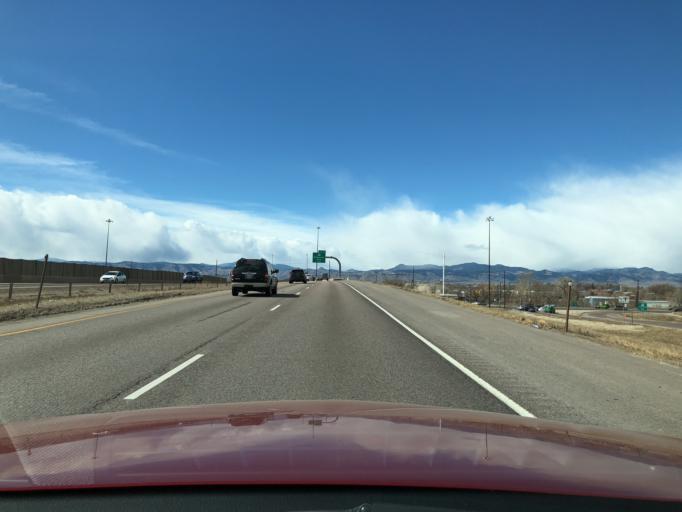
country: US
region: Colorado
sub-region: Adams County
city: Berkley
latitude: 39.7972
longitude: -105.0500
